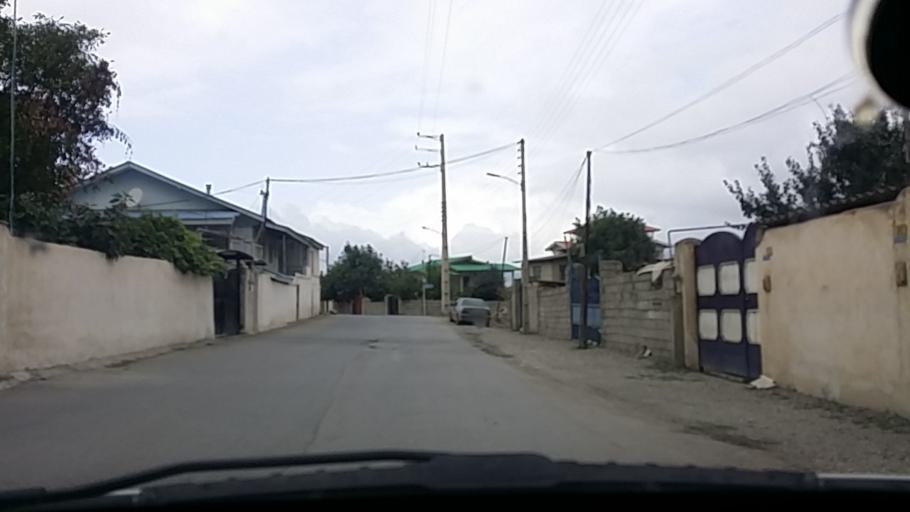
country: IR
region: Mazandaran
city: `Abbasabad
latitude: 36.5105
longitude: 51.1716
